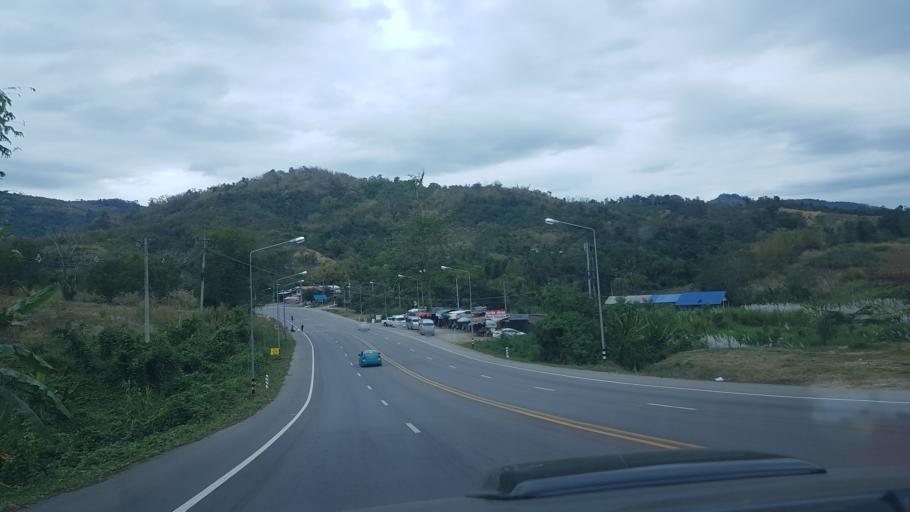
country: TH
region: Phetchabun
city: Khao Kho
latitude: 16.5424
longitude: 101.0549
